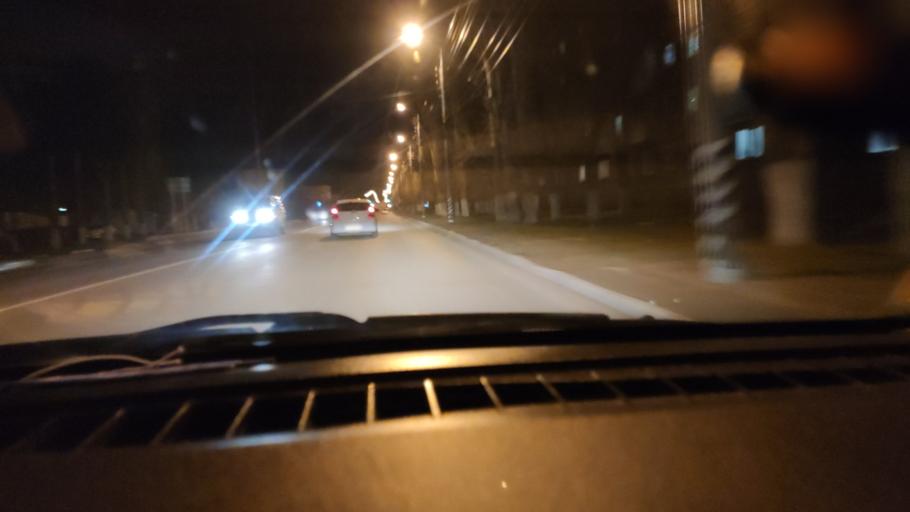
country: RU
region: Saratov
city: Privolzhskiy
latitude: 51.4090
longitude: 46.0410
